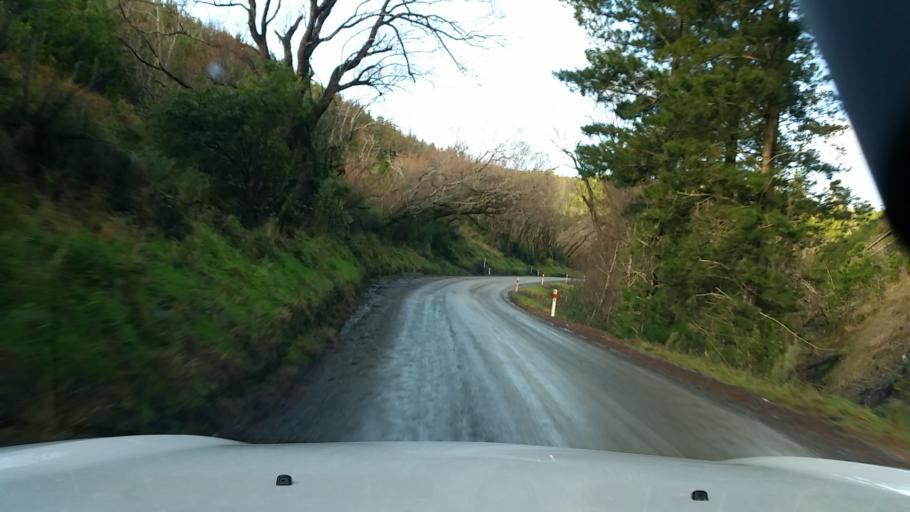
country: NZ
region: Wellington
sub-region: Masterton District
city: Masterton
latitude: -41.2252
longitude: 175.8579
